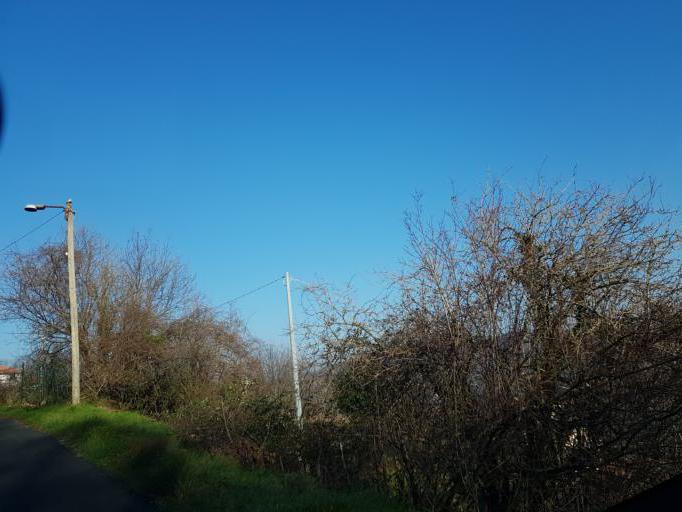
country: IT
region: Liguria
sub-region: Provincia di Genova
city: Manesseno
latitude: 44.4686
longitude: 8.9421
